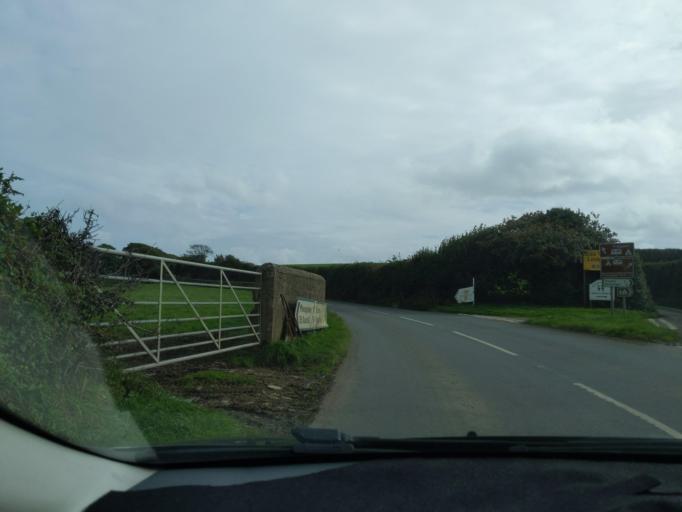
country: GB
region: England
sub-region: Cornwall
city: Mevagissey
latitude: 50.2494
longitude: -4.8198
